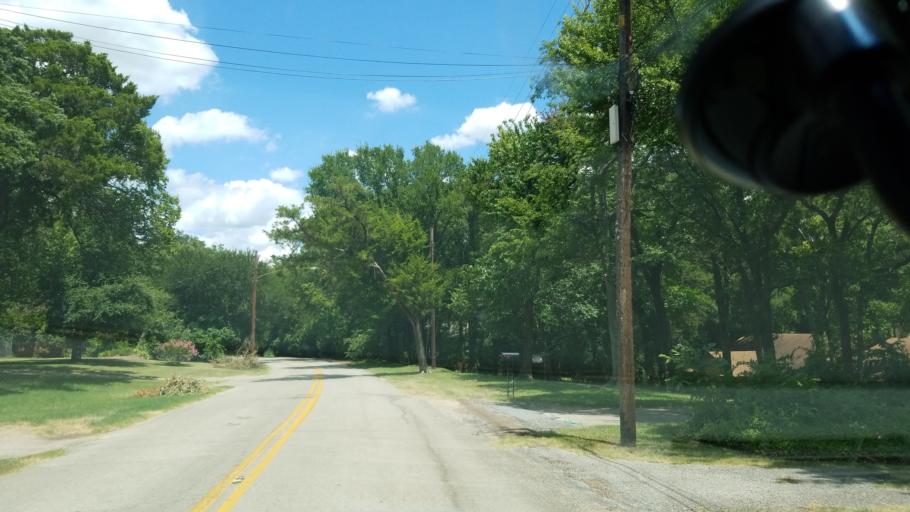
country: US
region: Texas
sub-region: Dallas County
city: Cockrell Hill
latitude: 32.6945
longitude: -96.8666
